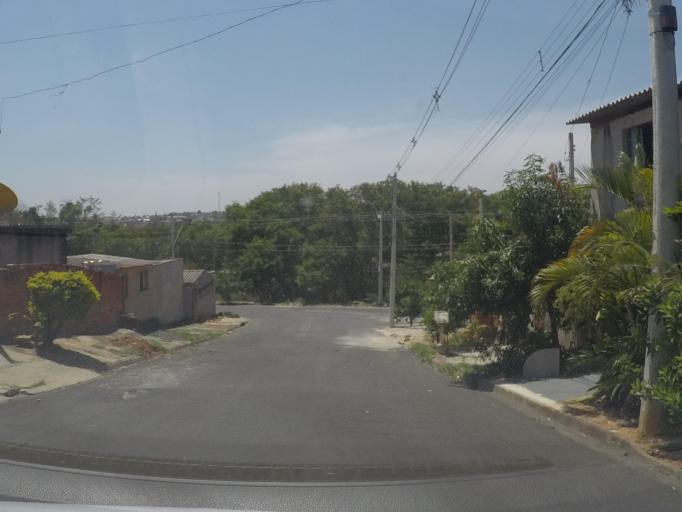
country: BR
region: Sao Paulo
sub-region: Hortolandia
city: Hortolandia
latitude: -22.8575
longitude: -47.1995
